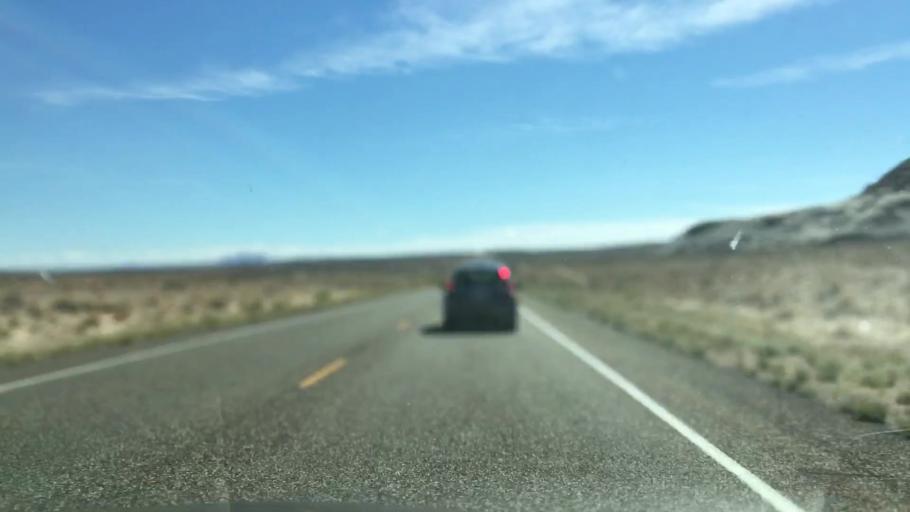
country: US
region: Arizona
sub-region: Coconino County
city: Page
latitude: 37.0242
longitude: -111.5977
